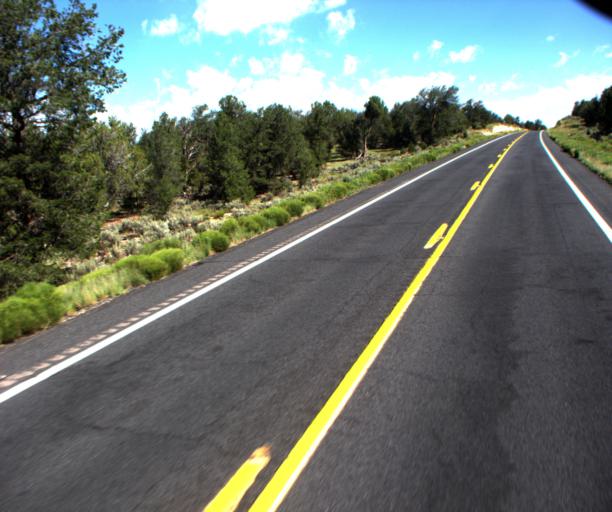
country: US
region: Arizona
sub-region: Coconino County
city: Grand Canyon Village
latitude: 35.8542
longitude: -112.1337
